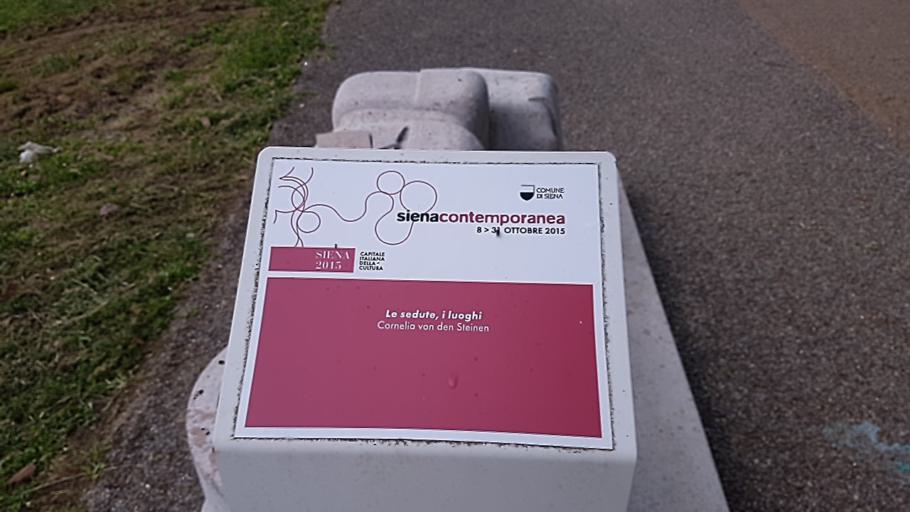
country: IT
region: Tuscany
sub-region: Provincia di Siena
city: Siena
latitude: 43.3237
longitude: 11.3167
